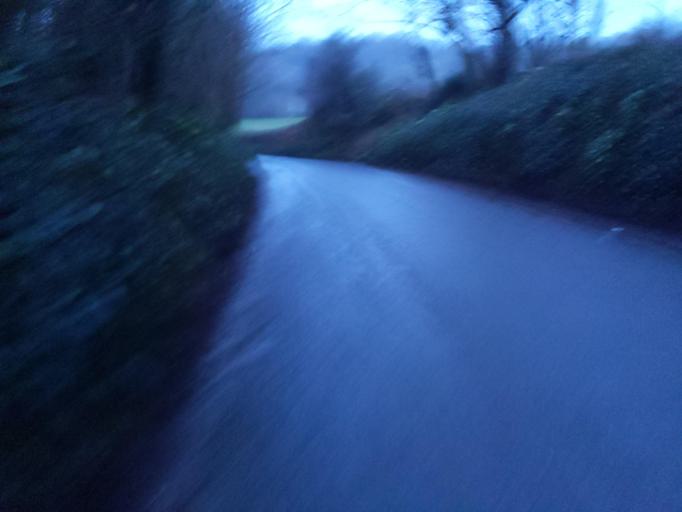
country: GB
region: England
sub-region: Devon
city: Yealmpton
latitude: 50.3390
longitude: -4.0114
